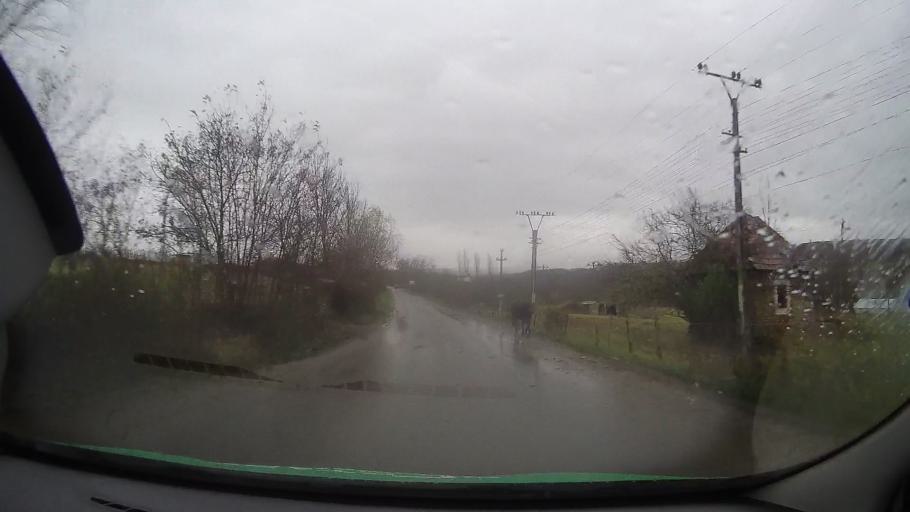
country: RO
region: Mures
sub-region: Comuna Brancovenesti
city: Valenii de Mures
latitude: 46.9248
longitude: 24.7712
